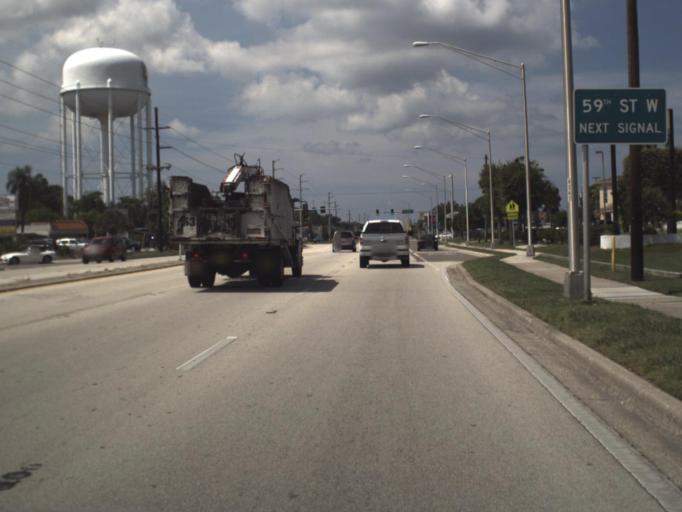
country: US
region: Florida
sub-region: Manatee County
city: South Bradenton
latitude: 27.4627
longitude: -82.6184
